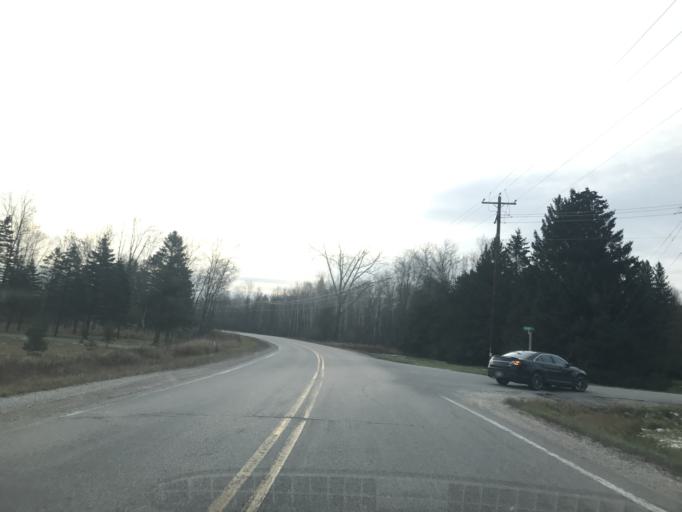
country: US
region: Wisconsin
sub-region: Marinette County
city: Peshtigo
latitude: 45.0586
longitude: -87.7938
